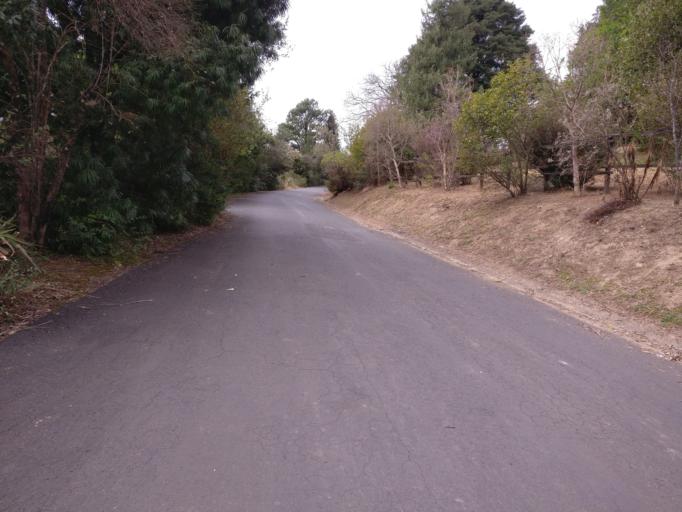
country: ZA
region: KwaZulu-Natal
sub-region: uThukela District Municipality
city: Bergville
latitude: -29.0136
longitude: 29.4172
